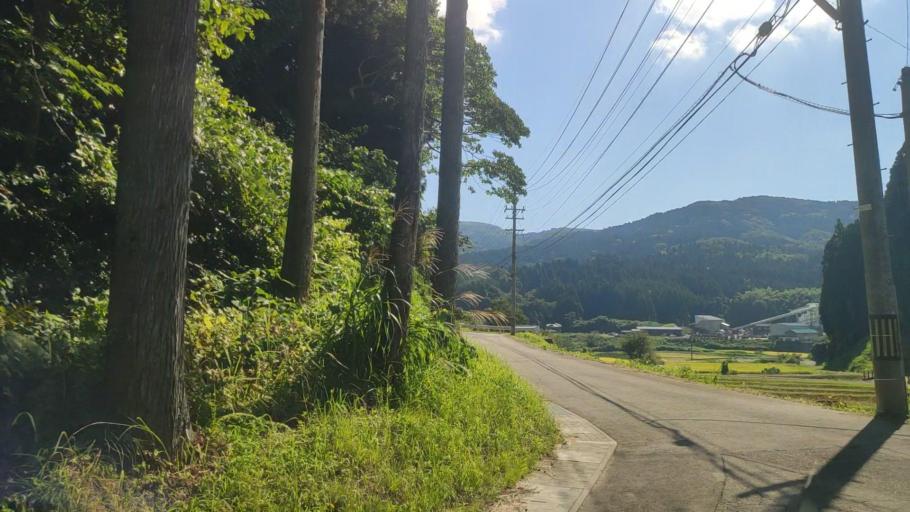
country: JP
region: Ishikawa
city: Nanao
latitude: 37.3696
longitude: 136.8668
